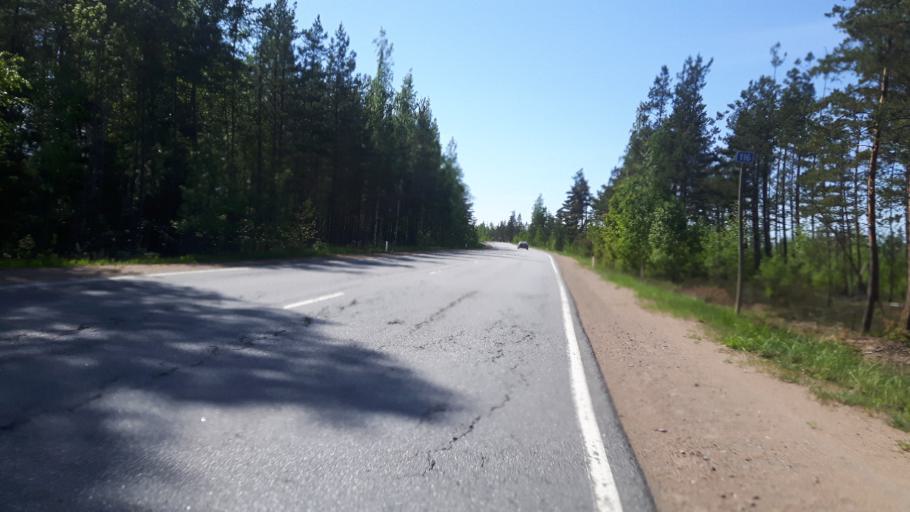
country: RU
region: Leningrad
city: Sista-Palkino
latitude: 59.7692
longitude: 28.7903
